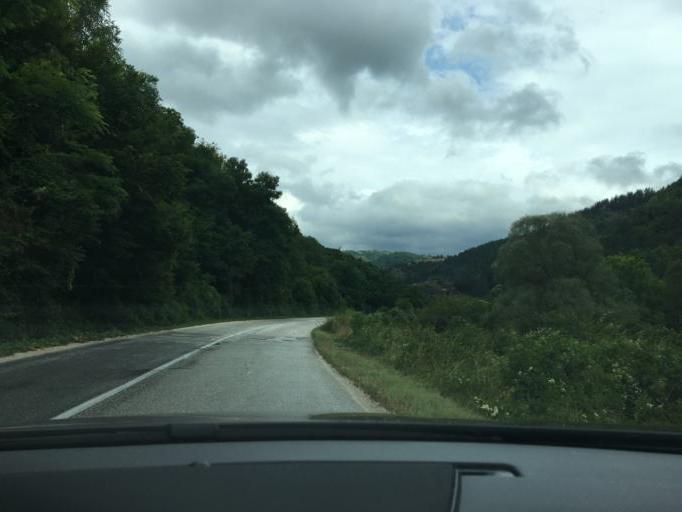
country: MK
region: Kriva Palanka
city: Kriva Palanka
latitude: 42.2265
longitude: 22.3860
